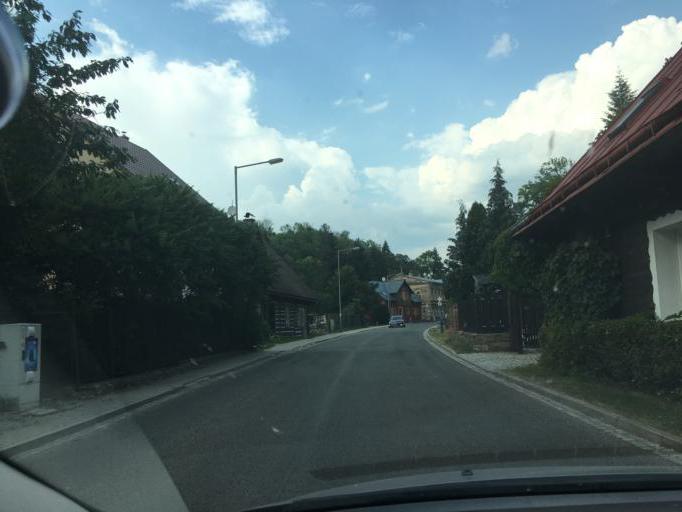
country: CZ
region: Kralovehradecky
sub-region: Okres Trutnov
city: Vrchlabi
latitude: 50.6351
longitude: 15.6073
